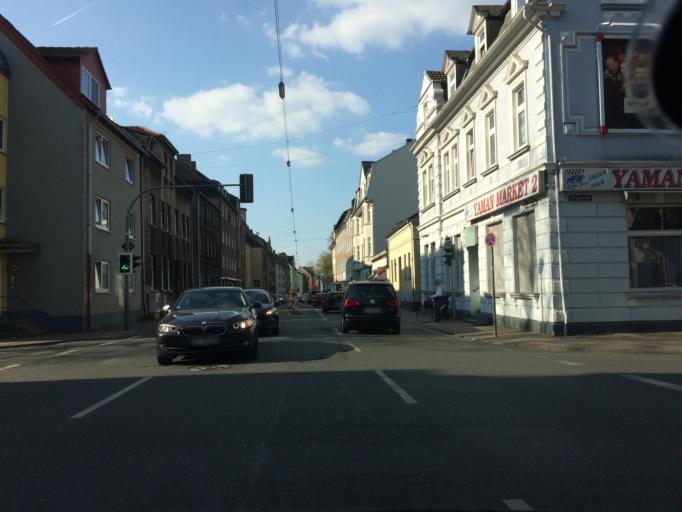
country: DE
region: North Rhine-Westphalia
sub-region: Regierungsbezirk Munster
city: Gelsenkirchen
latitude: 51.5015
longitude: 7.1184
